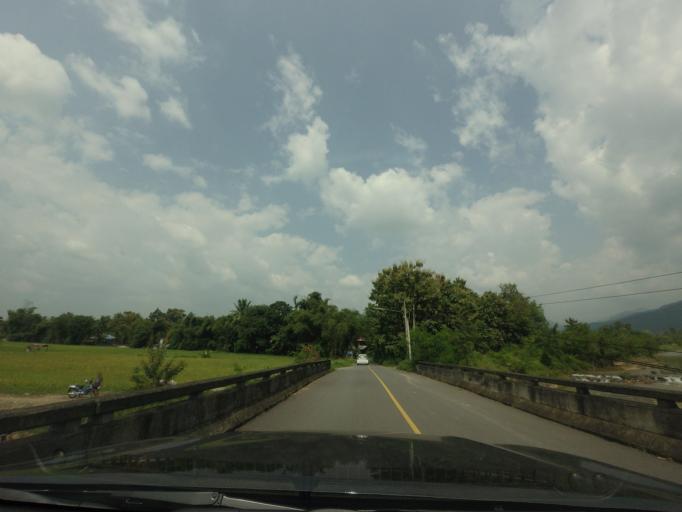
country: TH
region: Nan
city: Pua
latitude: 19.1684
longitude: 100.9377
